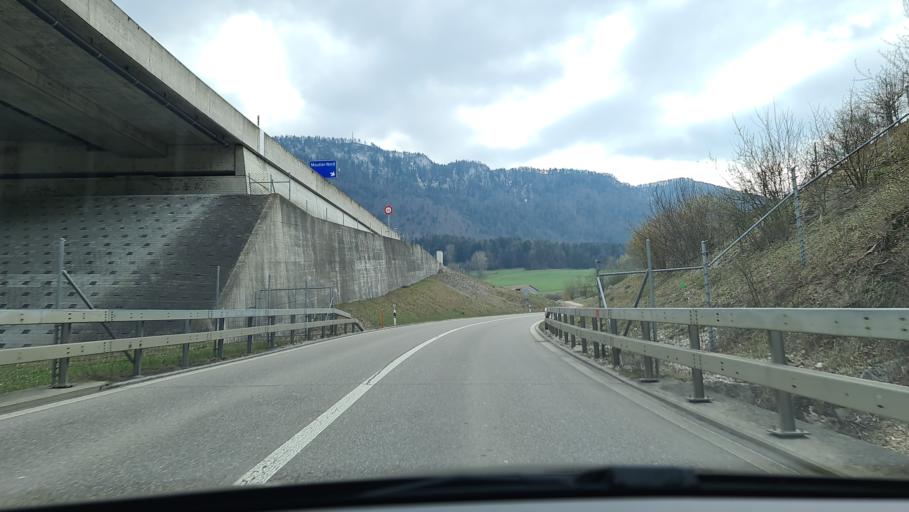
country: CH
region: Bern
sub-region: Jura bernois
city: Moutier
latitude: 47.2784
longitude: 7.3920
